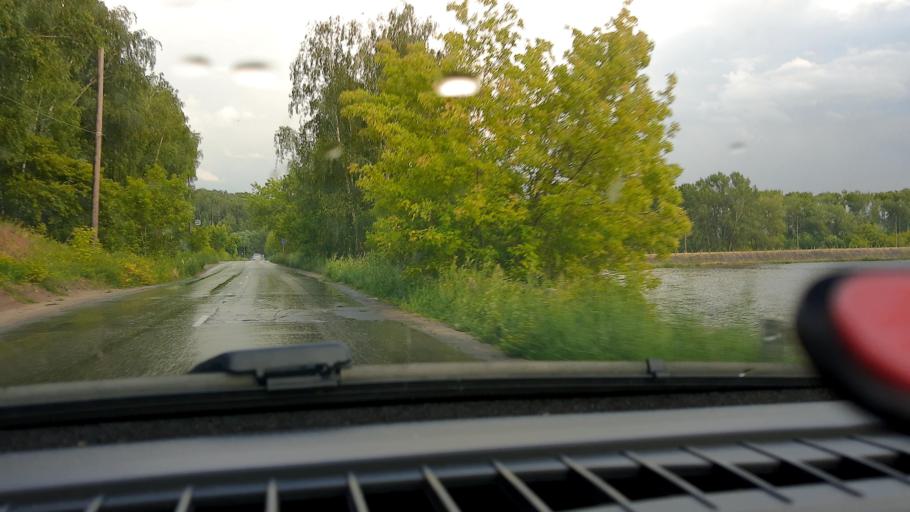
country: RU
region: Nizjnij Novgorod
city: Gorodets
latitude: 56.6697
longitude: 43.4513
